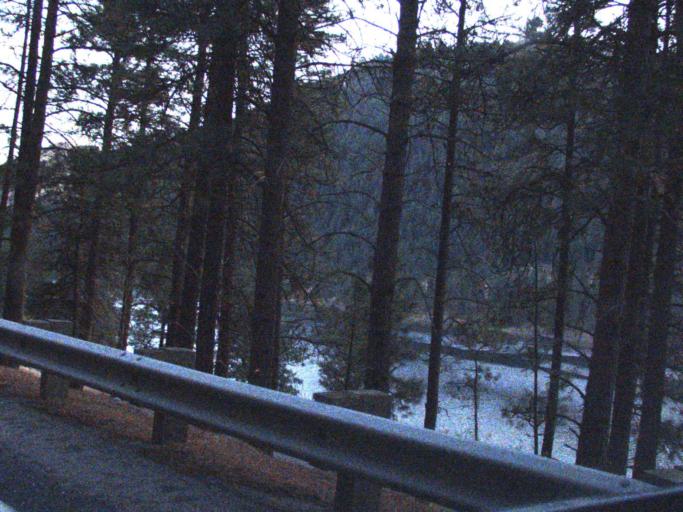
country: US
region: Washington
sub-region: Stevens County
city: Kettle Falls
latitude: 48.7270
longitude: -118.0433
